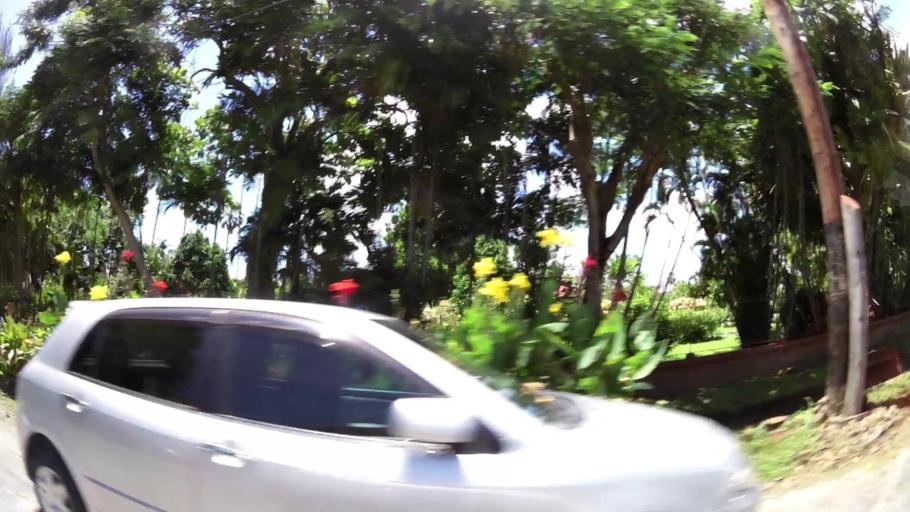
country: GY
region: Demerara-Mahaica
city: Georgetown
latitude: 6.8169
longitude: -58.1624
